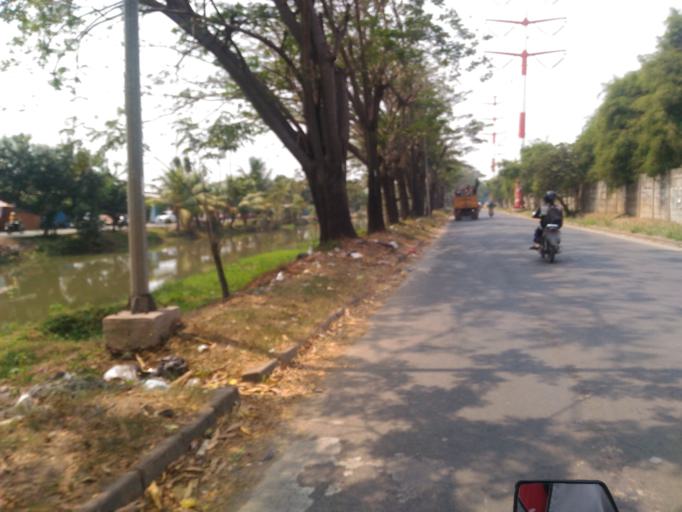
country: ID
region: West Java
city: Sepatan
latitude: -6.1485
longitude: 106.5934
